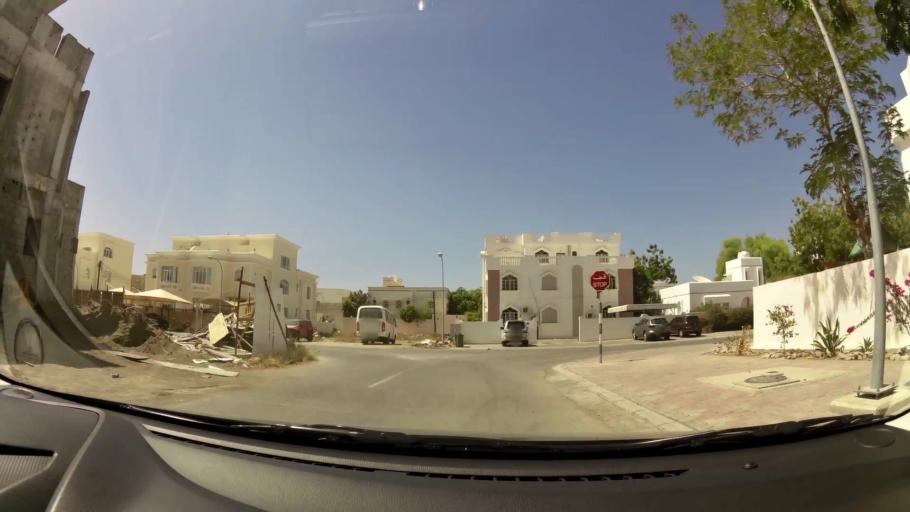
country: OM
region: Muhafazat Masqat
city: Bawshar
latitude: 23.5984
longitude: 58.3627
